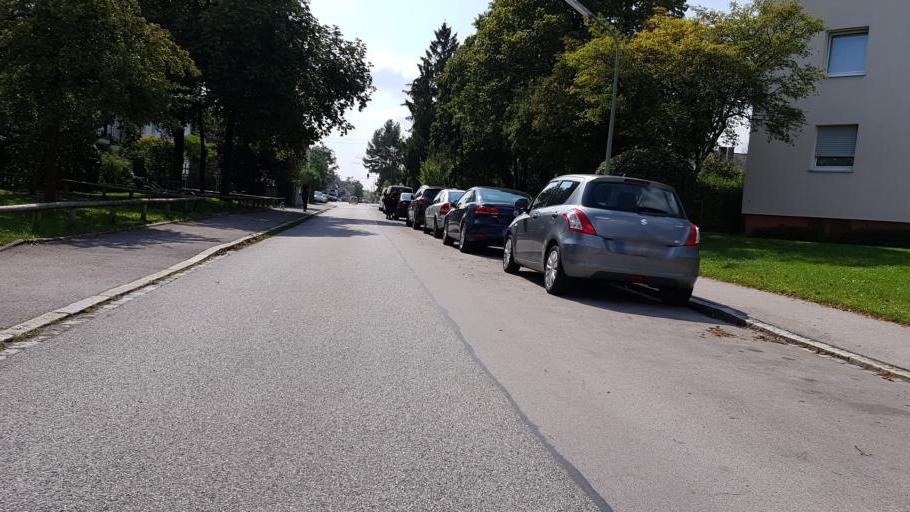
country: DE
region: Bavaria
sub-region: Upper Bavaria
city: Karlsfeld
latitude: 48.1844
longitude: 11.5092
